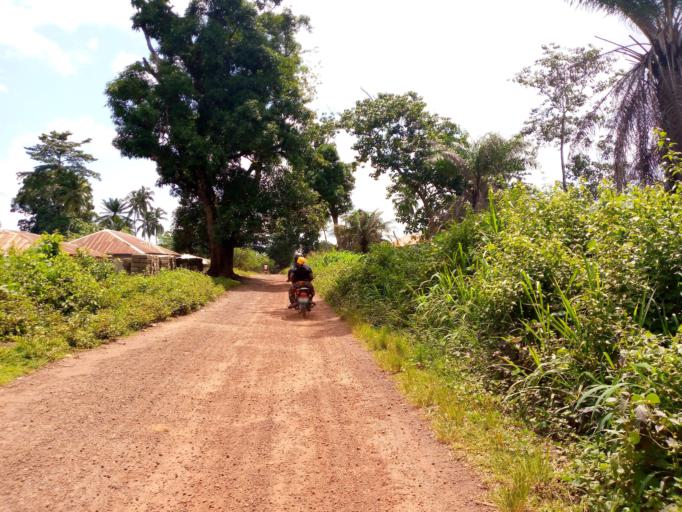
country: SL
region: Northern Province
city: Magburaka
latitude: 8.7094
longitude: -11.9287
